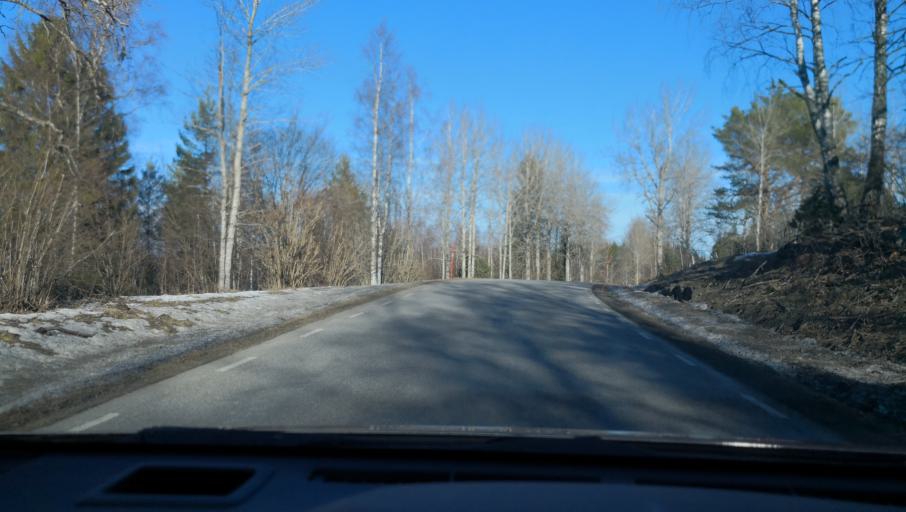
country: SE
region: Uppsala
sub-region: Osthammars Kommun
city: Osterbybruk
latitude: 60.2399
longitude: 17.9253
